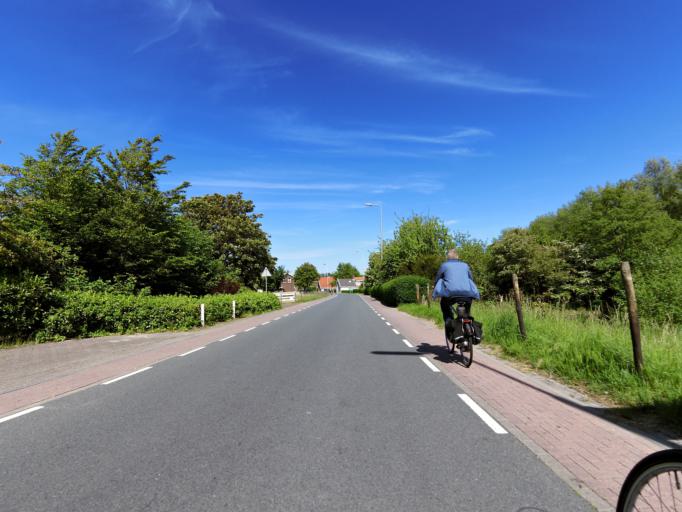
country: NL
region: South Holland
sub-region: Gemeente Hellevoetsluis
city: Nieuwenhoorn
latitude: 51.8575
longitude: 4.1485
